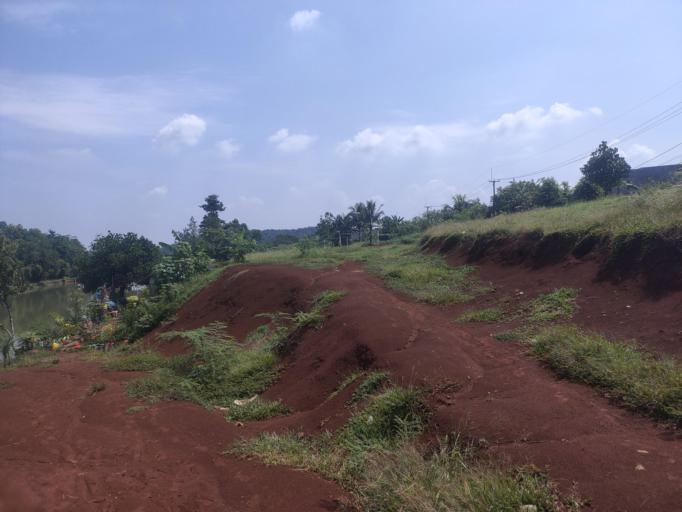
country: ID
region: West Java
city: Ciampea
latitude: -6.5261
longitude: 106.7005
